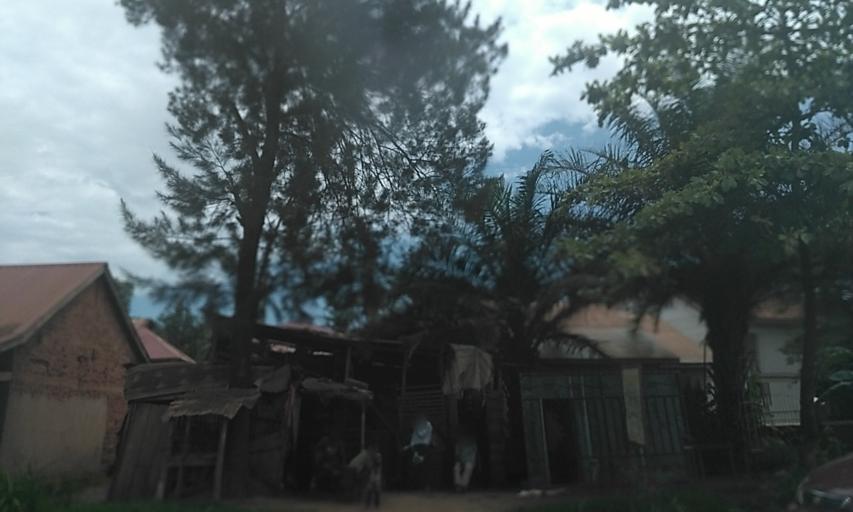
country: UG
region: Central Region
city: Kampala Central Division
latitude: 0.3191
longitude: 32.5220
